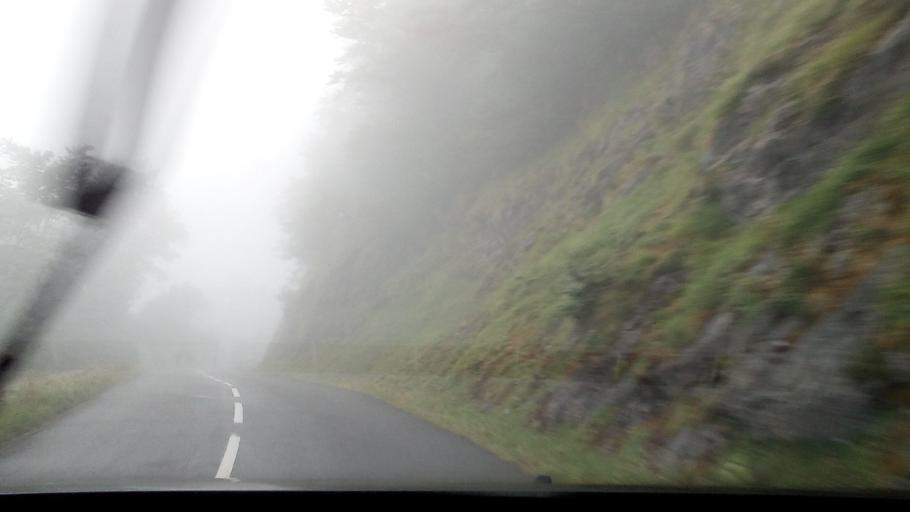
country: FR
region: Aquitaine
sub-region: Departement des Pyrenees-Atlantiques
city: Laruns
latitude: 42.9747
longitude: -0.3182
